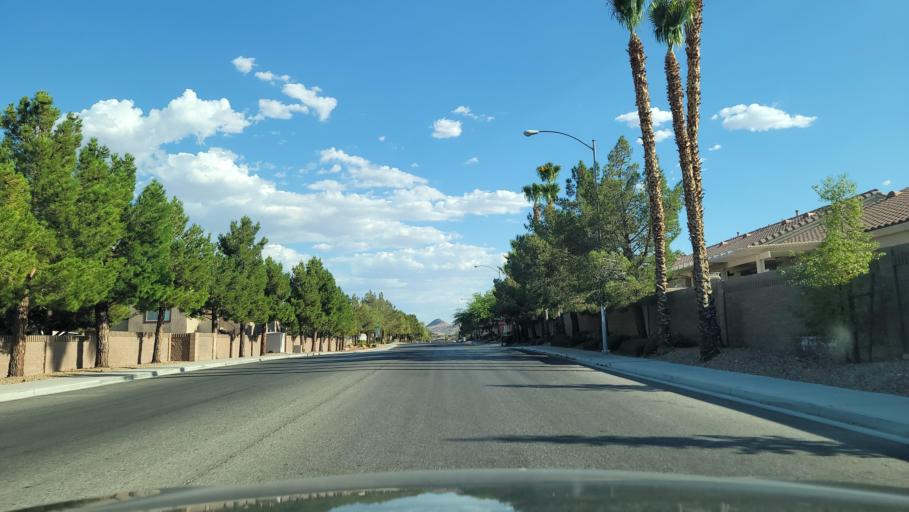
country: US
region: Nevada
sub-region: Clark County
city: Summerlin South
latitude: 36.0972
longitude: -115.3019
